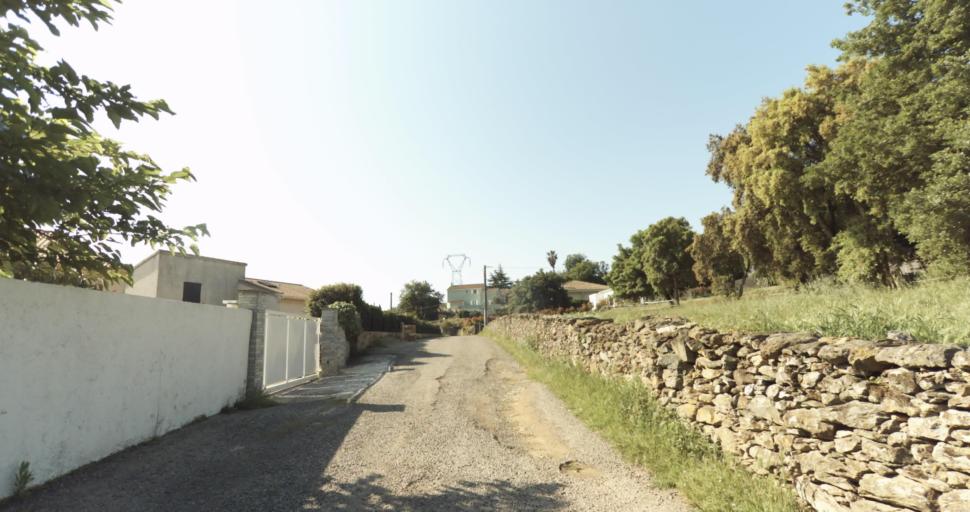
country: FR
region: Corsica
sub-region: Departement de la Haute-Corse
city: Biguglia
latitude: 42.6317
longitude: 9.4243
